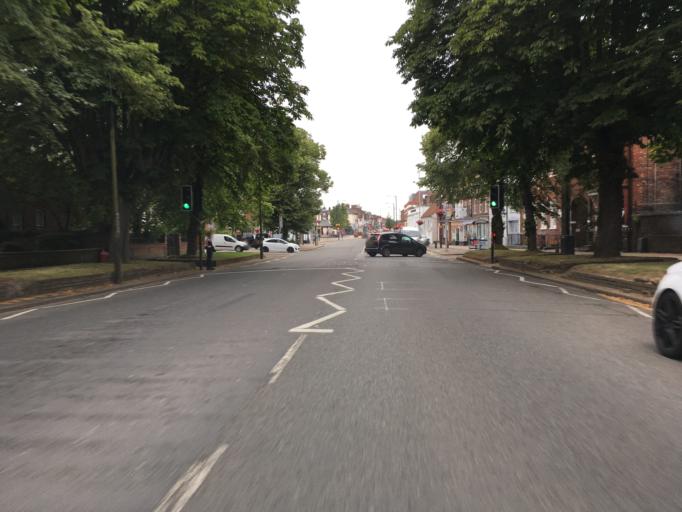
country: GB
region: England
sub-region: Central Bedfordshire
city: Dunstable
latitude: 51.8839
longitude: -0.5178
